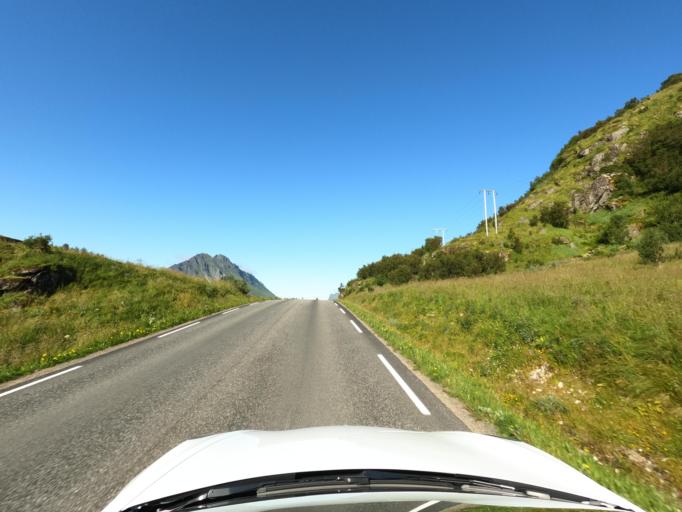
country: NO
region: Nordland
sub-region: Vagan
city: Kabelvag
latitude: 68.2263
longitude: 14.2207
